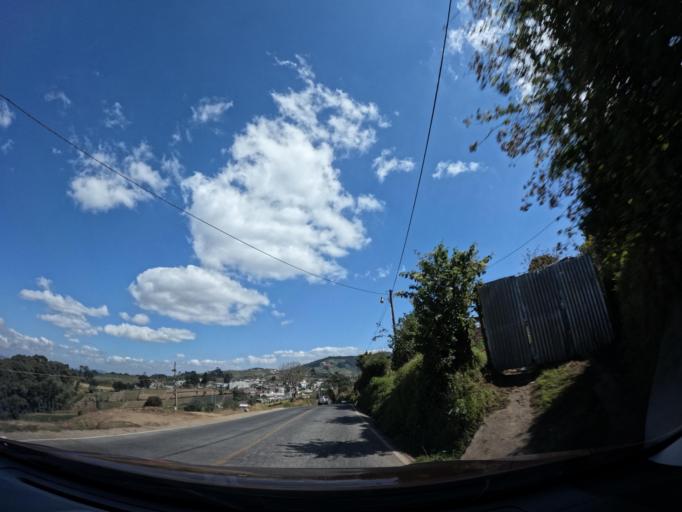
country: GT
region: Chimaltenango
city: Patzun
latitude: 14.6482
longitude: -91.0427
